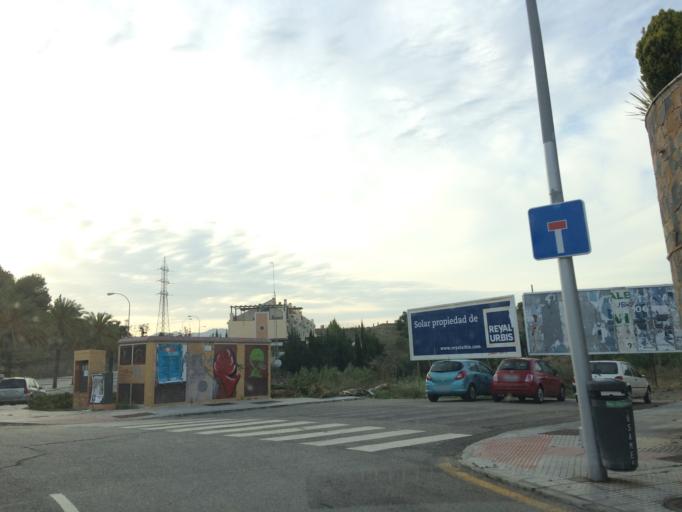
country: ES
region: Andalusia
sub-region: Provincia de Malaga
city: Malaga
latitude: 36.7303
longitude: -4.3901
